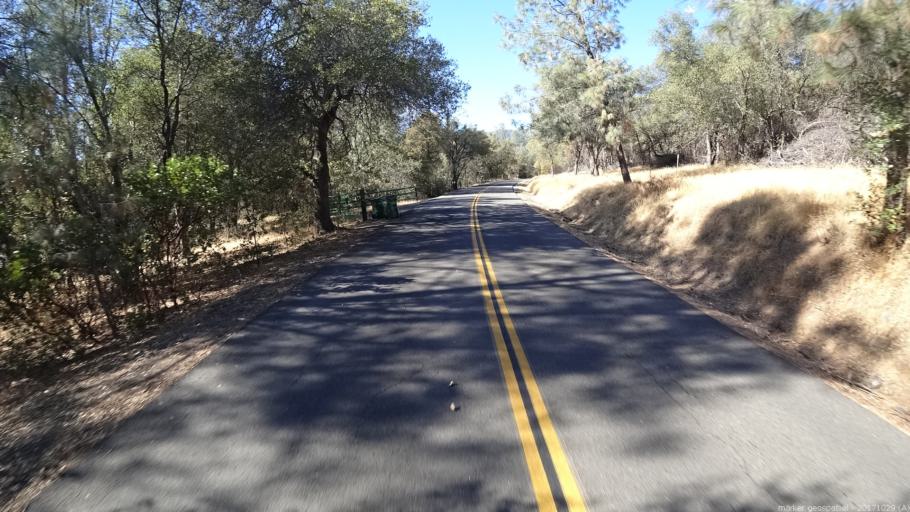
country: US
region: California
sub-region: Shasta County
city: Shasta
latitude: 40.4783
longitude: -122.6485
